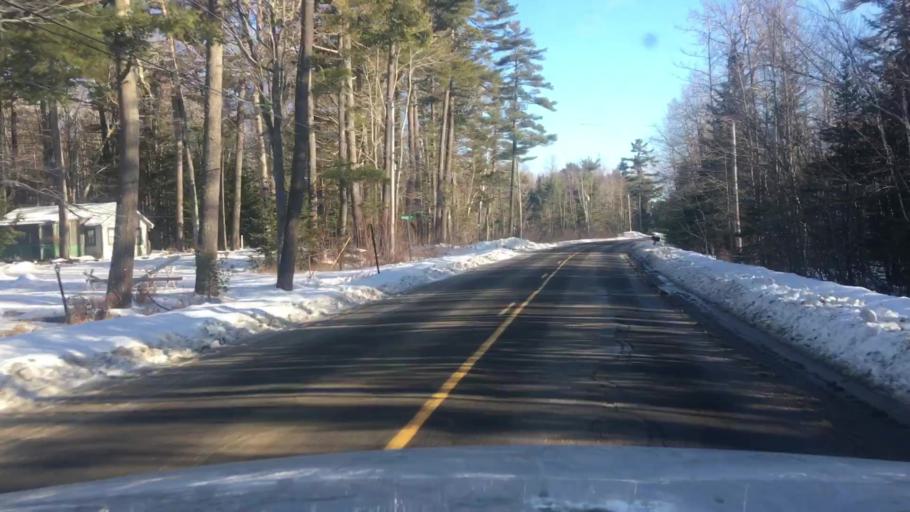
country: US
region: Maine
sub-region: Hancock County
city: Ellsworth
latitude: 44.6165
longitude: -68.3854
